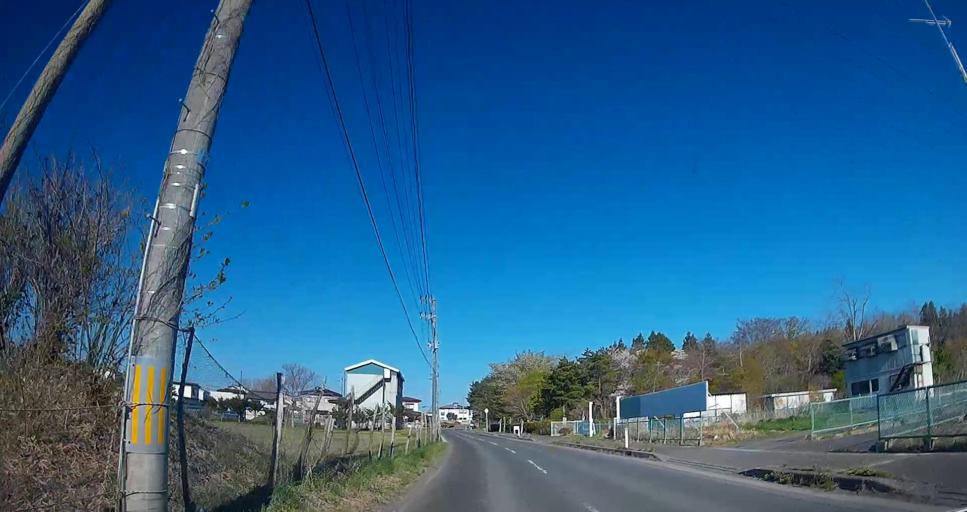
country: JP
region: Aomori
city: Hachinohe
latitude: 40.5197
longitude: 141.5774
